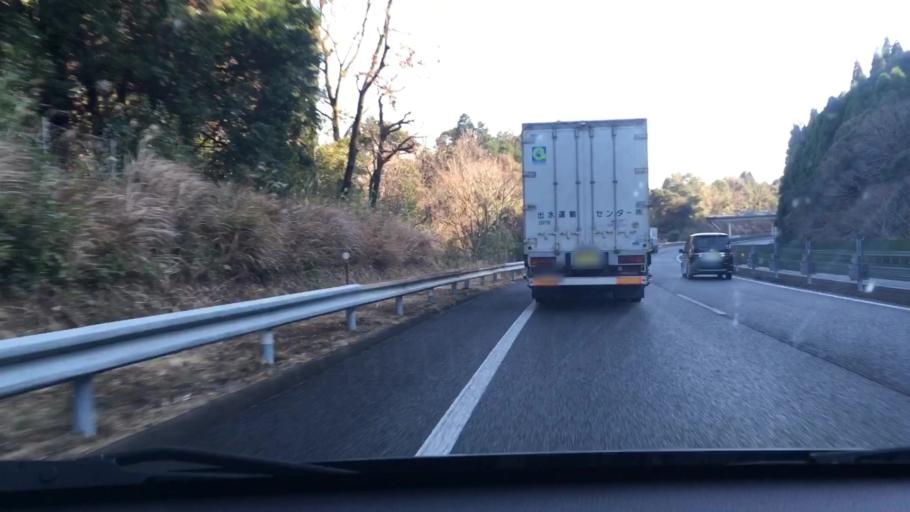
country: JP
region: Kagoshima
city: Kajiki
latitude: 31.8311
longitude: 130.6931
